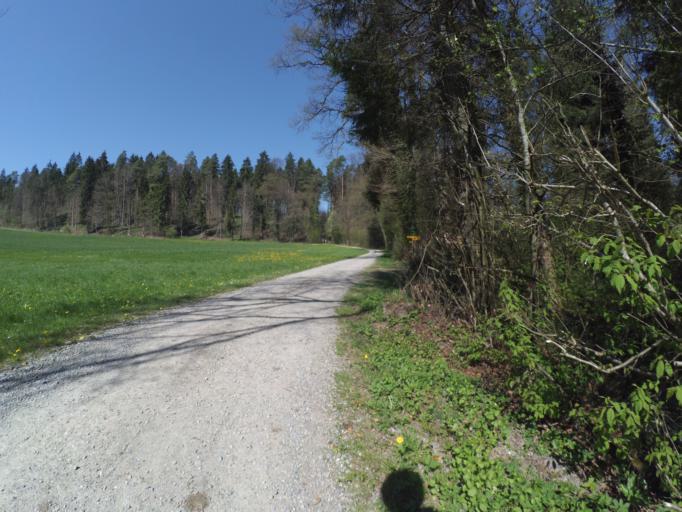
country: CH
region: Thurgau
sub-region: Frauenfeld District
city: Frauenfeld
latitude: 47.5925
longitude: 8.9104
